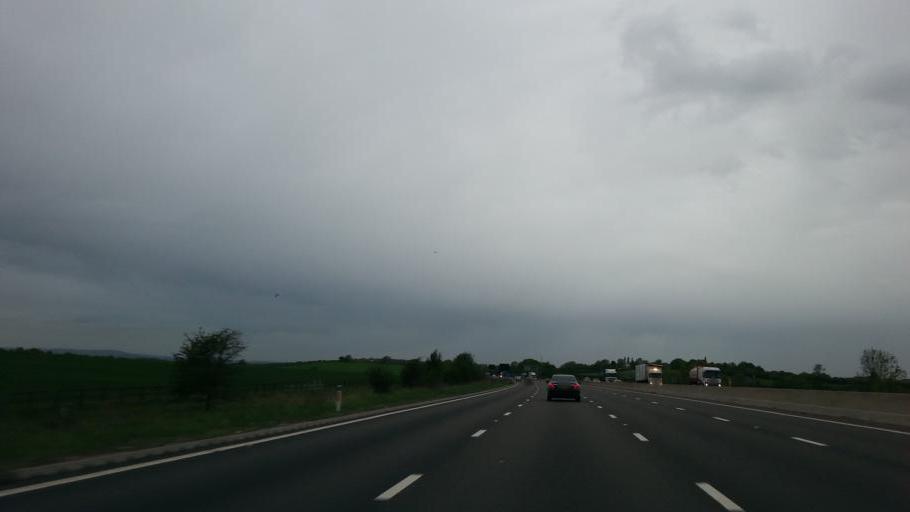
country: GB
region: England
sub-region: Rotherham
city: Wales
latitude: 53.3282
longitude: -1.2824
